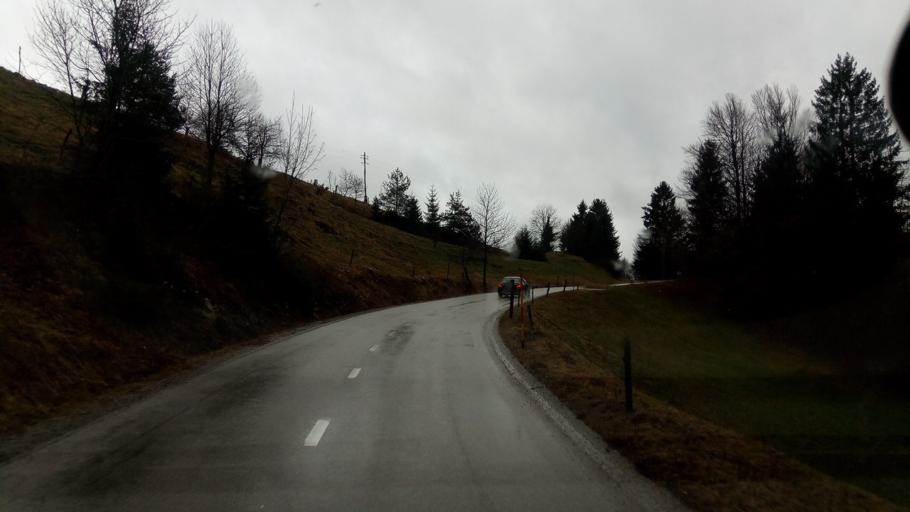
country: SI
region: Horjul
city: Horjul
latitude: 46.0165
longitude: 14.2152
